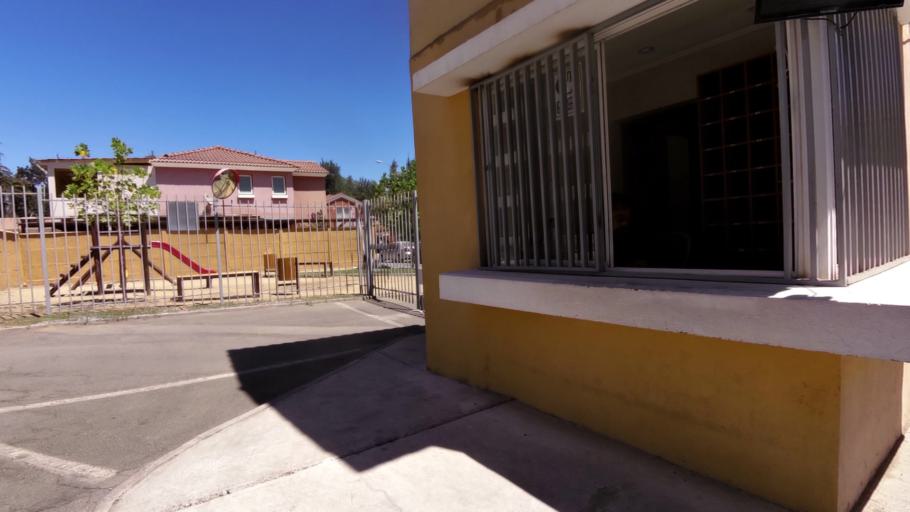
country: CL
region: O'Higgins
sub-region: Provincia de Cachapoal
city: Rancagua
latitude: -34.1654
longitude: -70.7535
